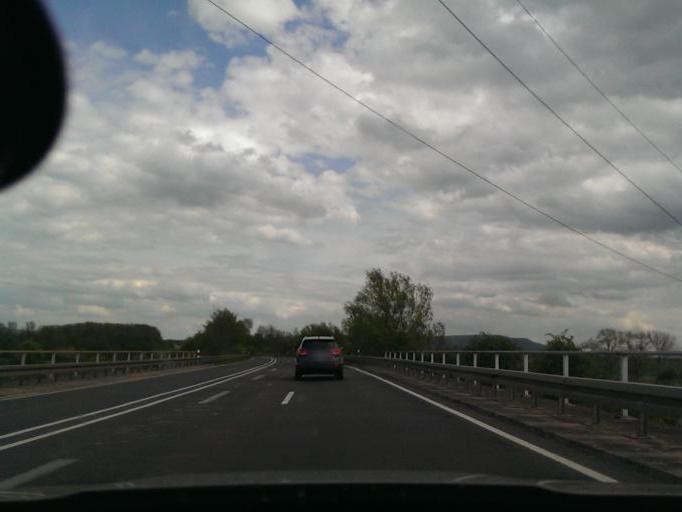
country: DE
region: Lower Saxony
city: Elze
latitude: 52.1079
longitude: 9.7262
